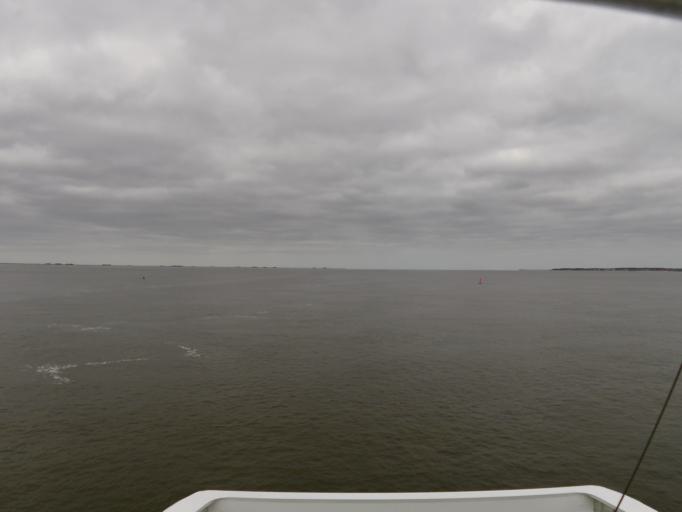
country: DE
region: Schleswig-Holstein
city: Dagebull
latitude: 54.6997
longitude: 8.6371
